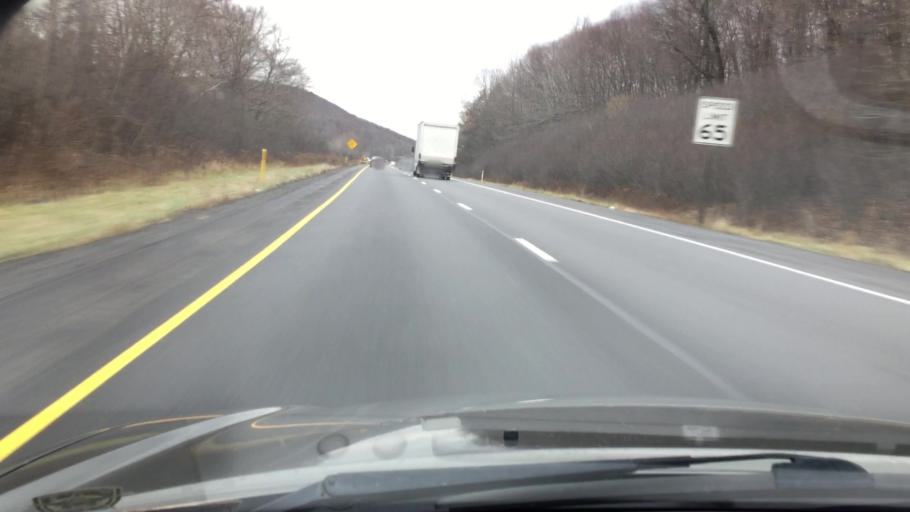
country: US
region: Pennsylvania
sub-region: Luzerne County
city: White Haven
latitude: 41.0574
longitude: -75.7879
